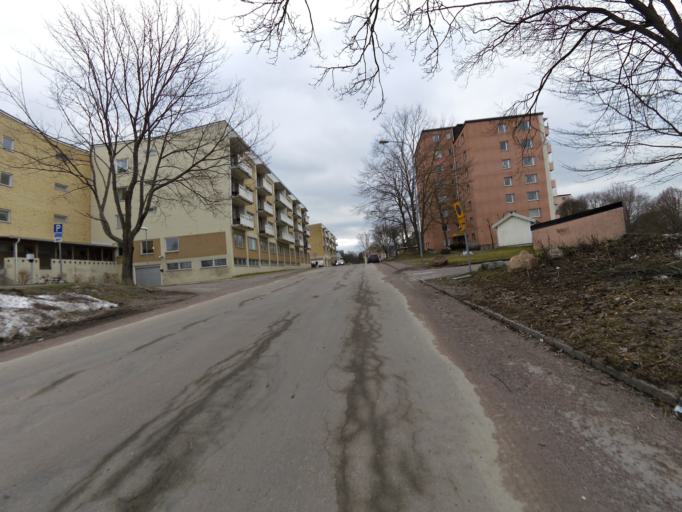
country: SE
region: Gaevleborg
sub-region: Gavle Kommun
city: Gavle
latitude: 60.6768
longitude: 17.1740
